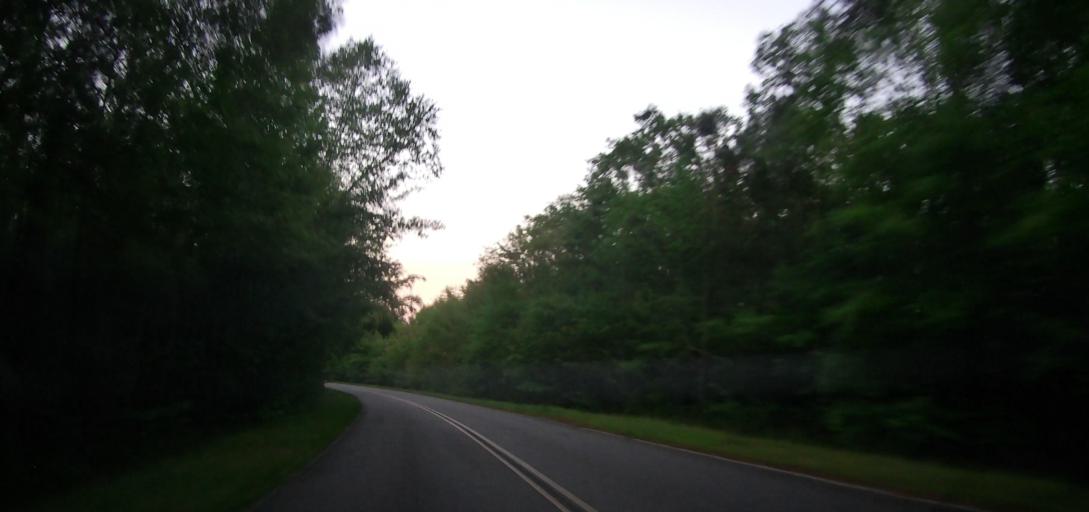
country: US
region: Georgia
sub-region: Marion County
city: Buena Vista
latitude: 32.2542
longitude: -84.5844
